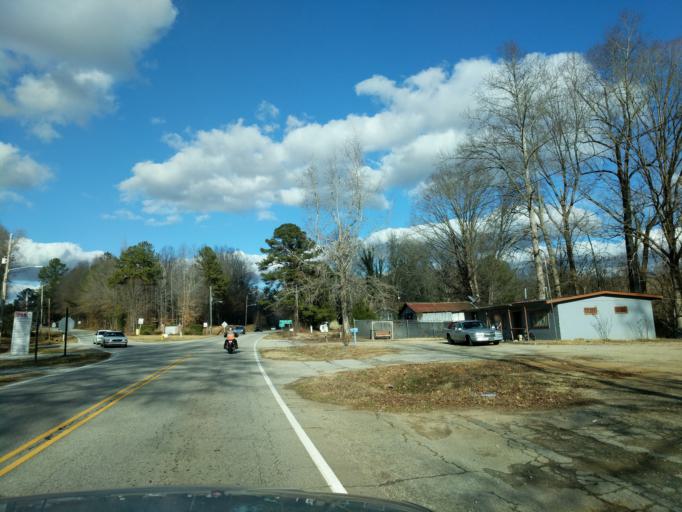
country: US
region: South Carolina
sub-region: Laurens County
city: Laurens
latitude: 34.4754
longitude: -82.0280
